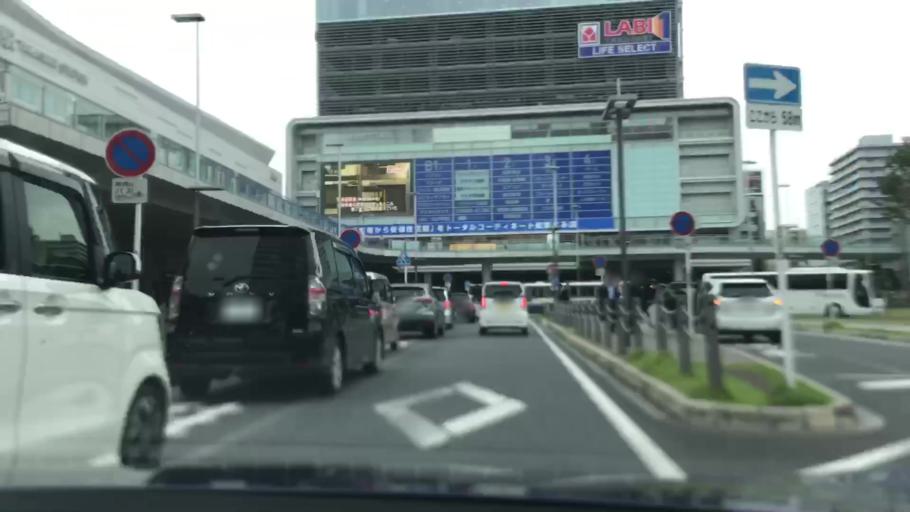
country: JP
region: Gunma
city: Takasaki
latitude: 36.3216
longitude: 139.0139
